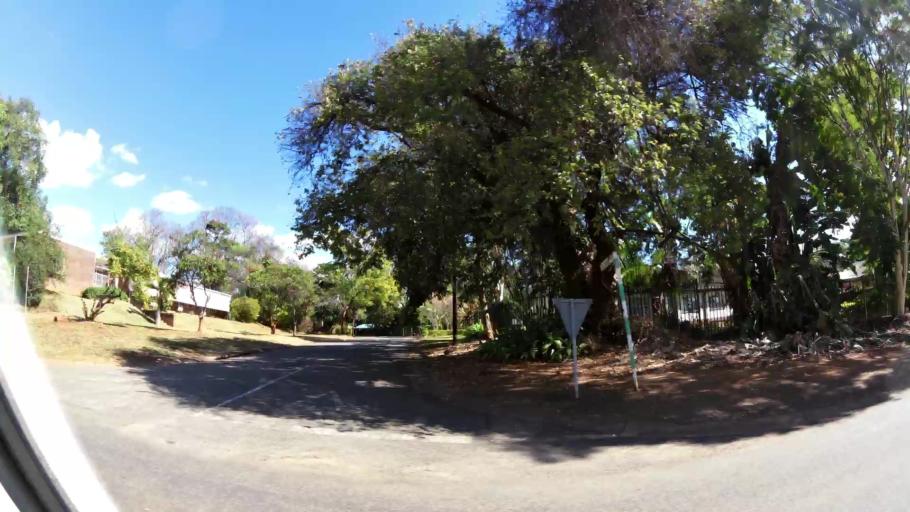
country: ZA
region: Limpopo
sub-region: Mopani District Municipality
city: Tzaneen
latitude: -23.8327
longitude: 30.1523
